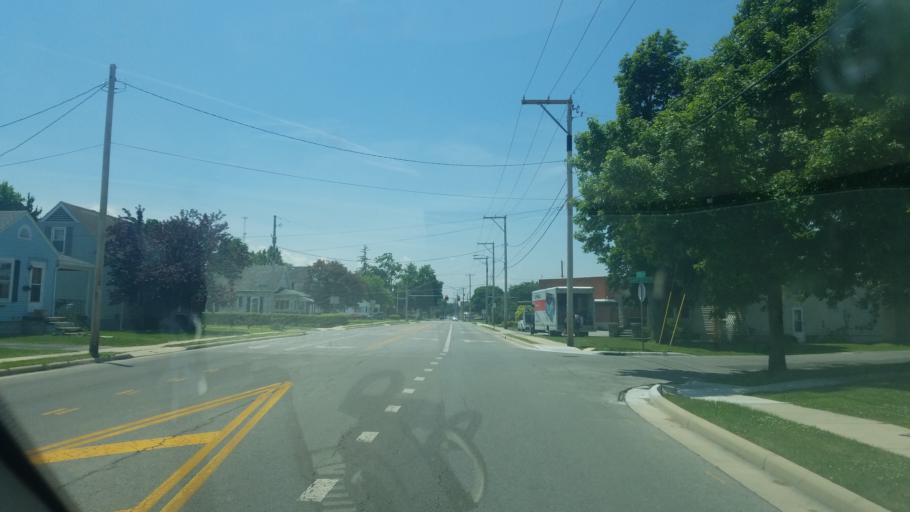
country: US
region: Ohio
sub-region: Hancock County
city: Findlay
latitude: 41.0550
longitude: -83.6404
